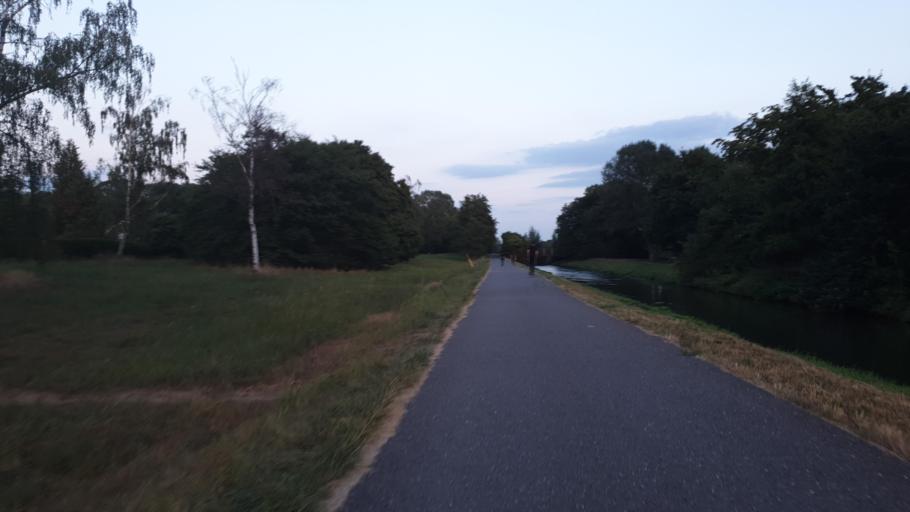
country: DE
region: North Rhine-Westphalia
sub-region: Regierungsbezirk Koln
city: Bergheim
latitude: 50.9445
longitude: 6.6399
